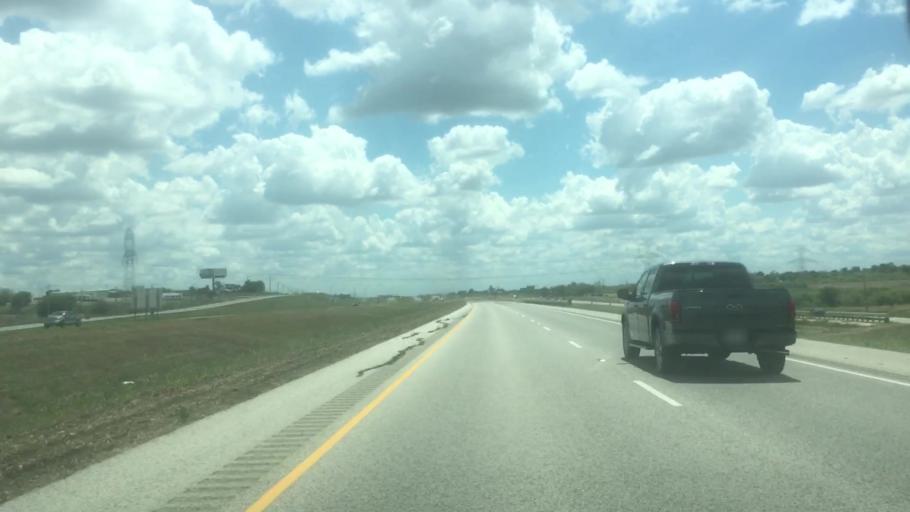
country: US
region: Texas
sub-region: Caldwell County
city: Uhland
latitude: 29.9992
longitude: -97.6866
